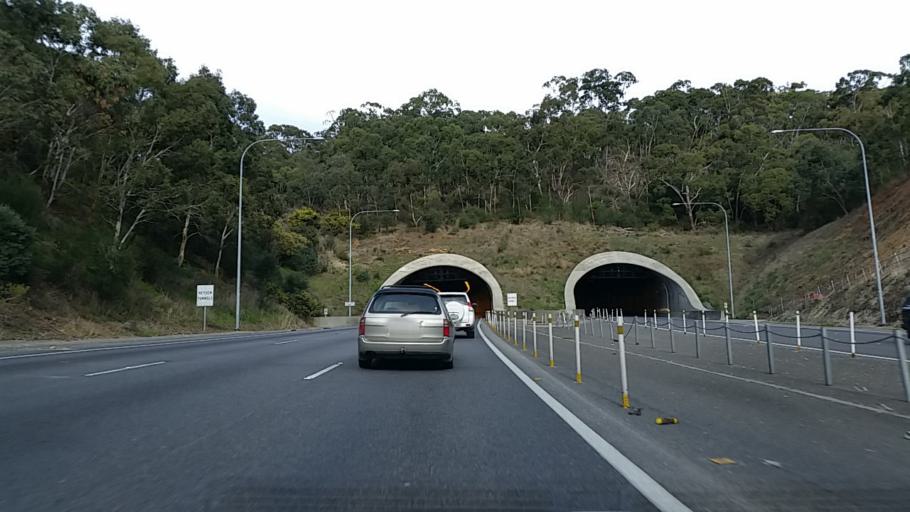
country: AU
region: South Australia
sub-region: Burnside
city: Mount Osmond
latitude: -34.9721
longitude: 138.6763
